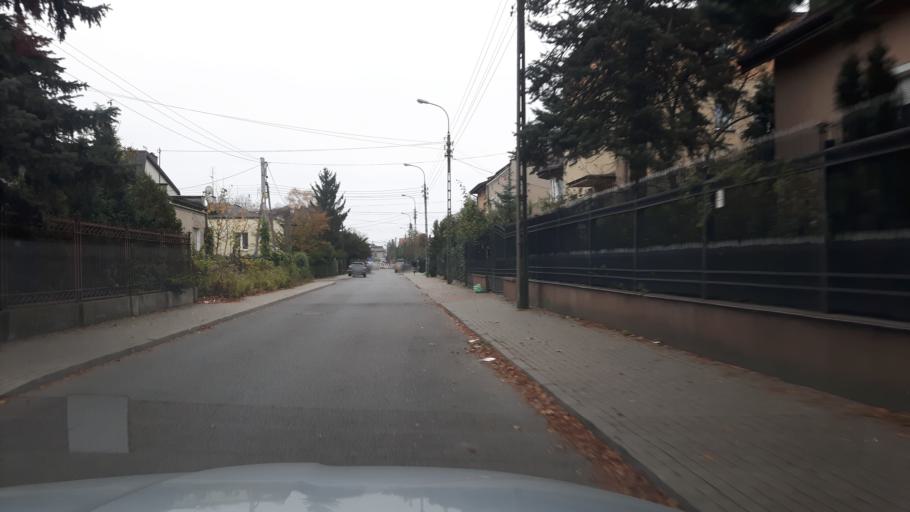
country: PL
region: Masovian Voivodeship
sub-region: Warszawa
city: Targowek
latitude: 52.2774
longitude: 21.0661
